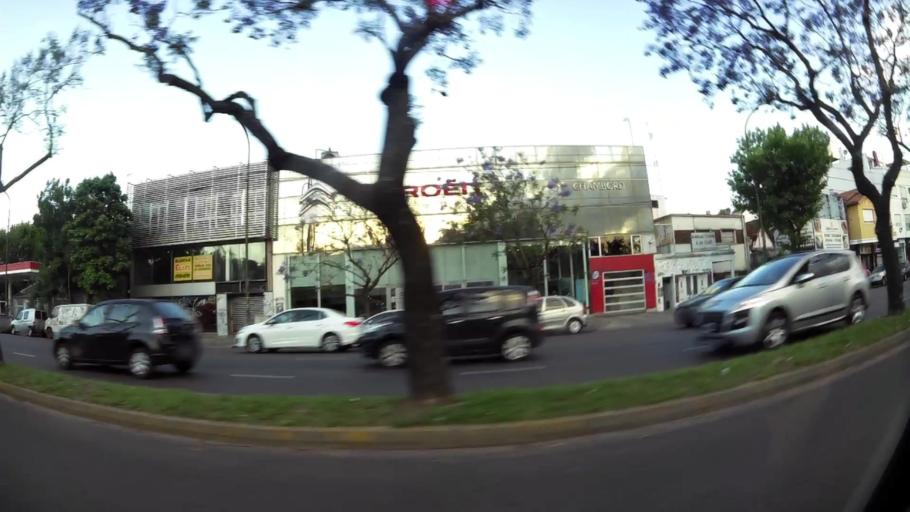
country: AR
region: Buenos Aires
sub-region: Partido de Vicente Lopez
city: Olivos
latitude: -34.4936
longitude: -58.4984
